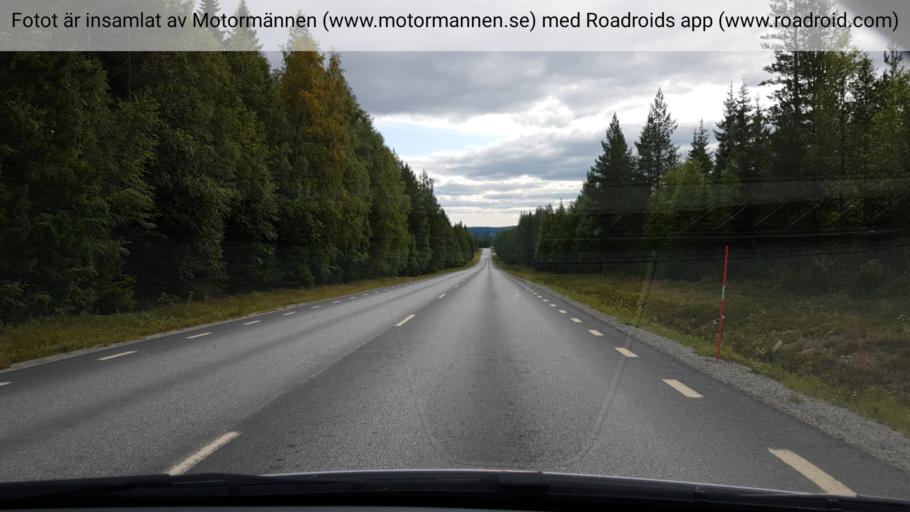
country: SE
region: Vaesterbotten
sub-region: Vannas Kommun
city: Vannasby
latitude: 64.0415
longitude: 20.0054
